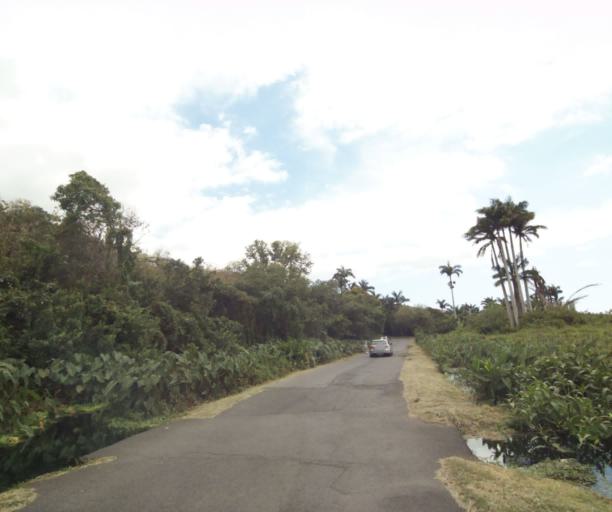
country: RE
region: Reunion
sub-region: Reunion
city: Saint-Paul
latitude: -20.9998
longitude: 55.3019
